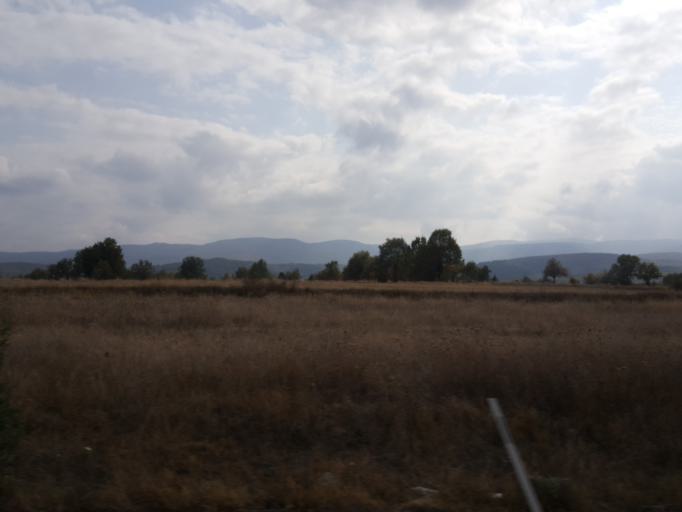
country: TR
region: Sinop
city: Sarayduzu
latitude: 41.3303
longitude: 34.7716
